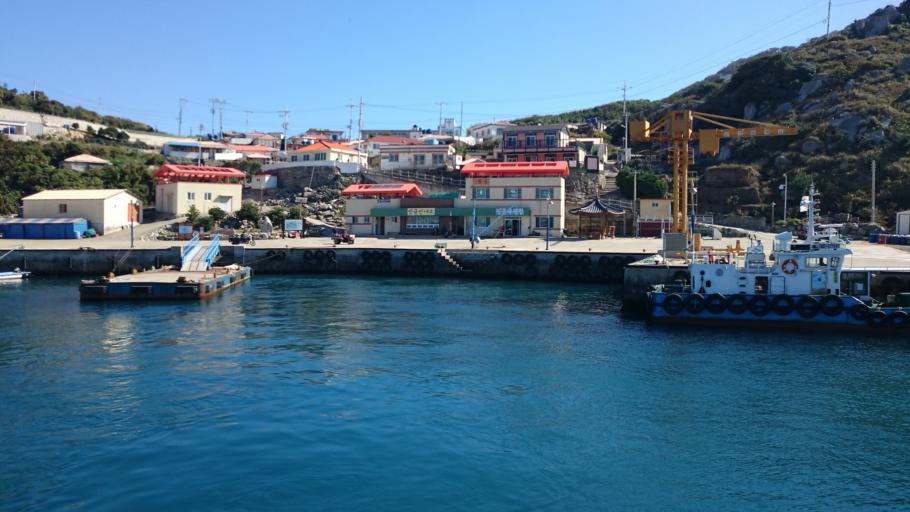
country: KR
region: Gyeongsangnam-do
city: Kyosai
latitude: 34.6478
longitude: 128.5743
